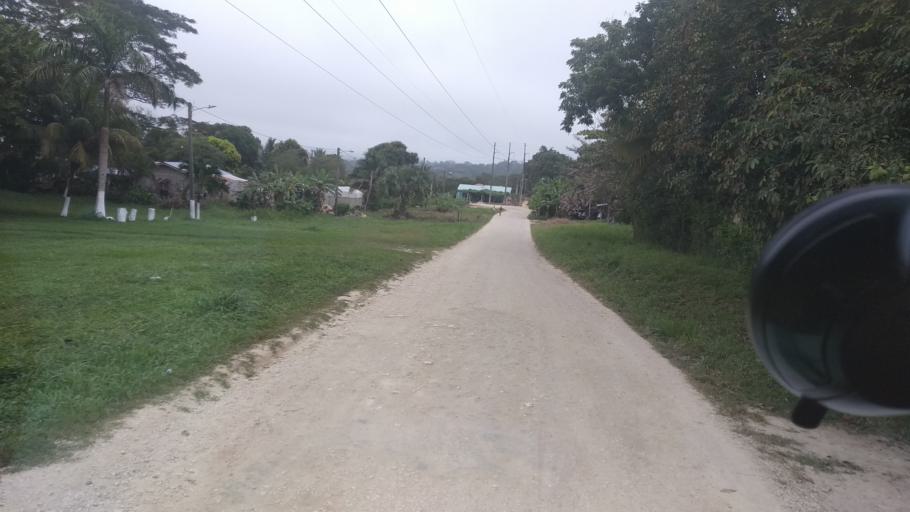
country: BZ
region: Cayo
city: Benque Viejo del Carmen
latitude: 17.0817
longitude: -89.1245
